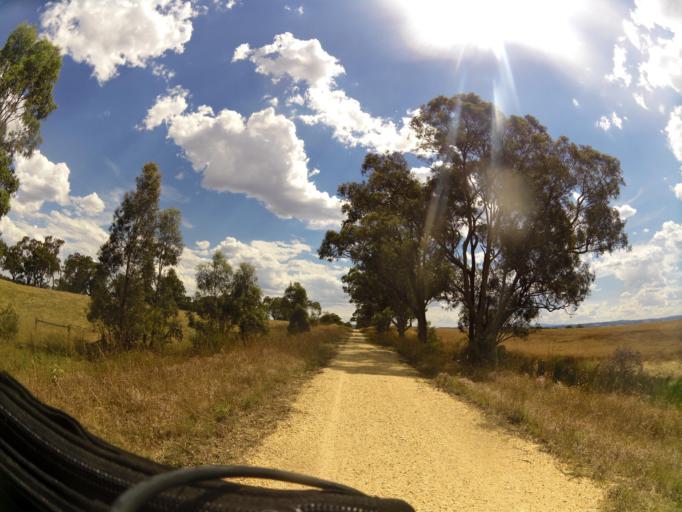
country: AU
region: Victoria
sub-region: Wellington
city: Heyfield
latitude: -37.9787
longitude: 146.7489
